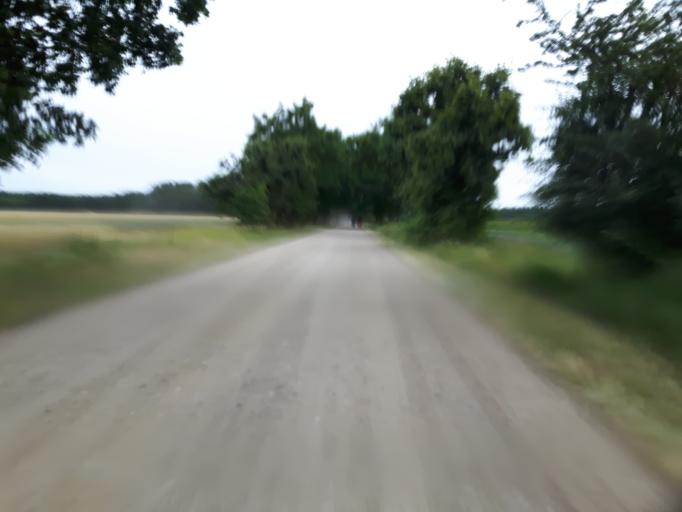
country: DE
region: Lower Saxony
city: Winsen
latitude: 53.3230
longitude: 10.1980
